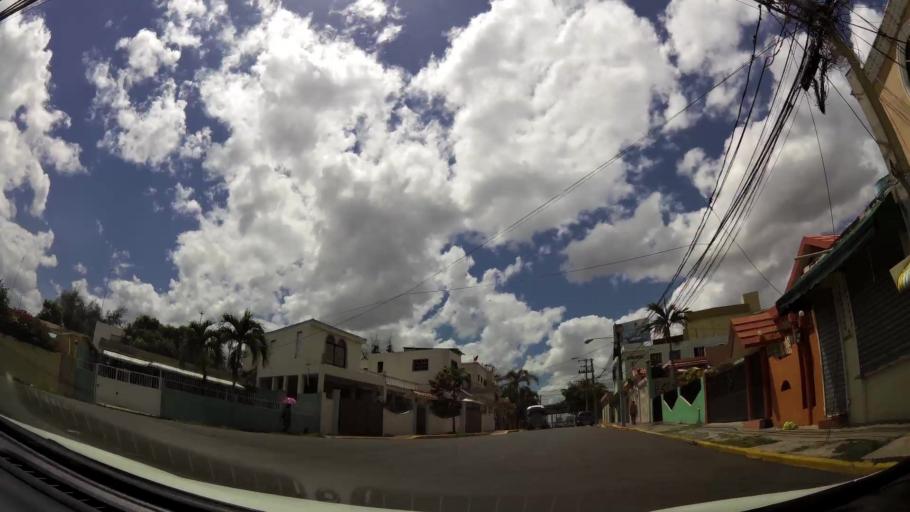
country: DO
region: Nacional
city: Ensanche Luperon
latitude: 18.5214
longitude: -69.9146
